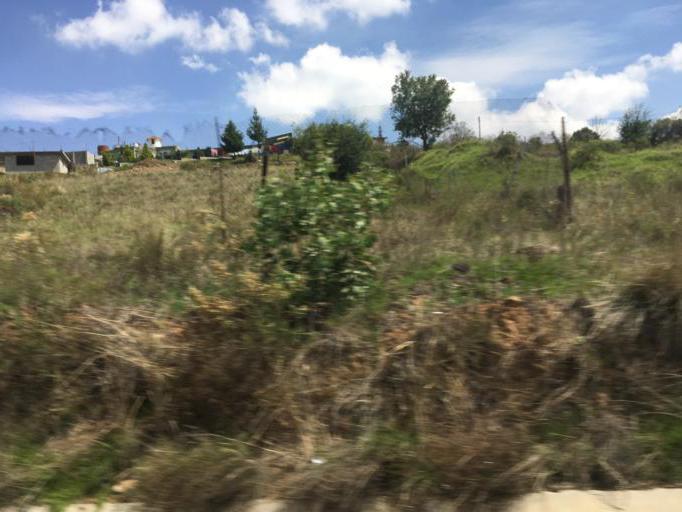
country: MX
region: Mexico
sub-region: Timilpan
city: Tercera Manzana de Zaragoza
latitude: 19.8830
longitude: -99.6576
